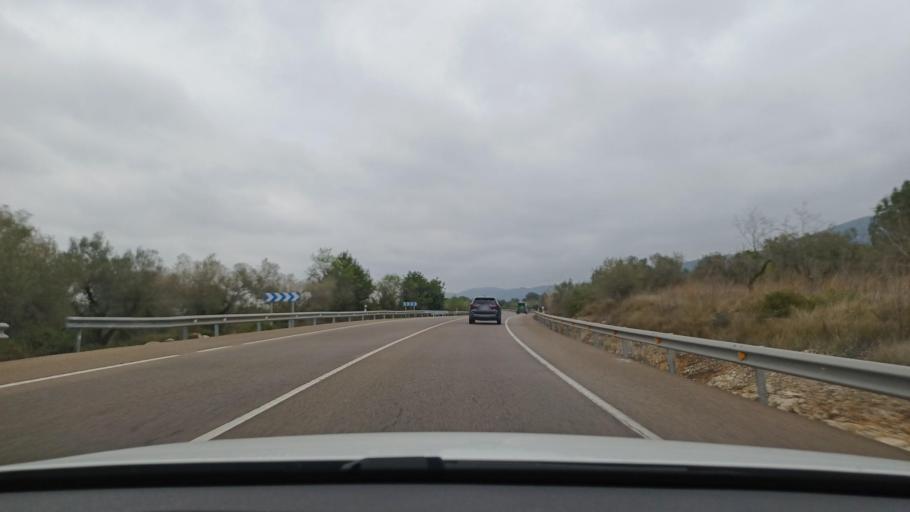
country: ES
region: Valencia
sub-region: Provincia de Castello
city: Santa Magdalena de Pulpis
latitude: 40.3422
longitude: 0.2684
